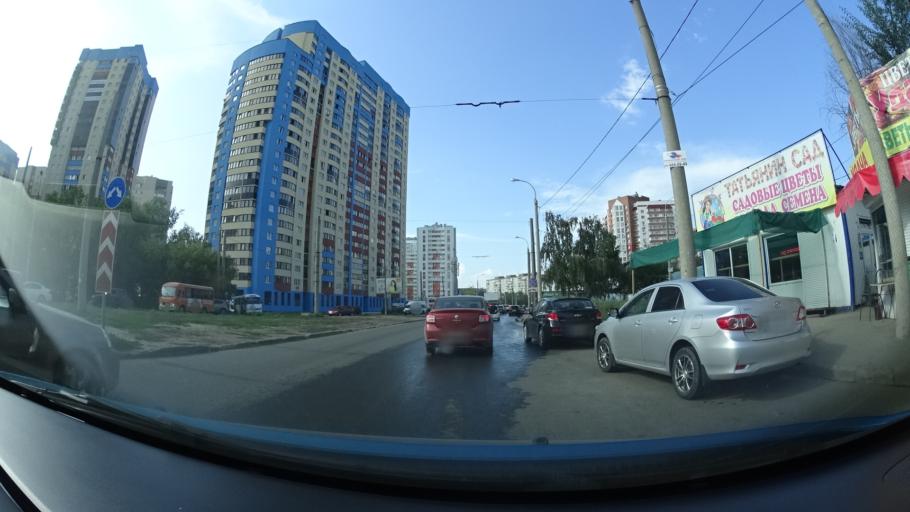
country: RU
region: Samara
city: Samara
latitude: 53.2592
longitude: 50.2249
